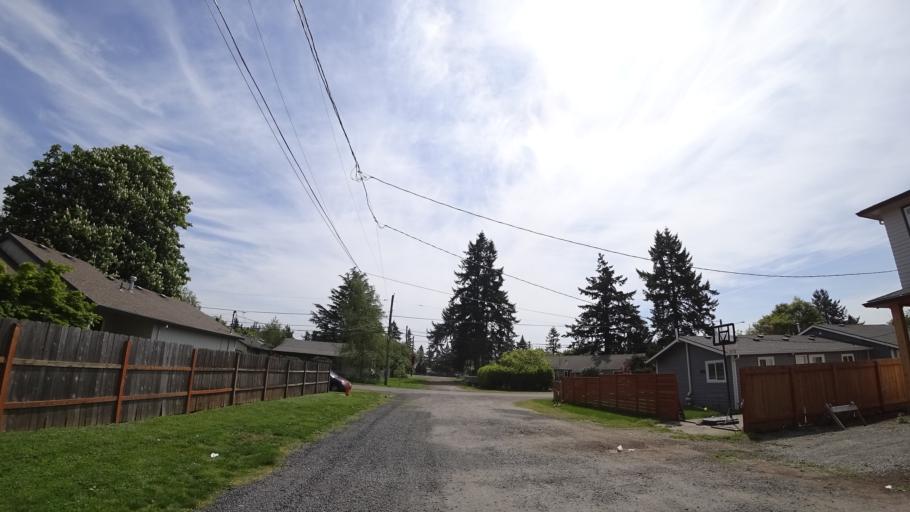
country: US
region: Oregon
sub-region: Clackamas County
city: Milwaukie
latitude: 45.4669
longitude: -122.6074
